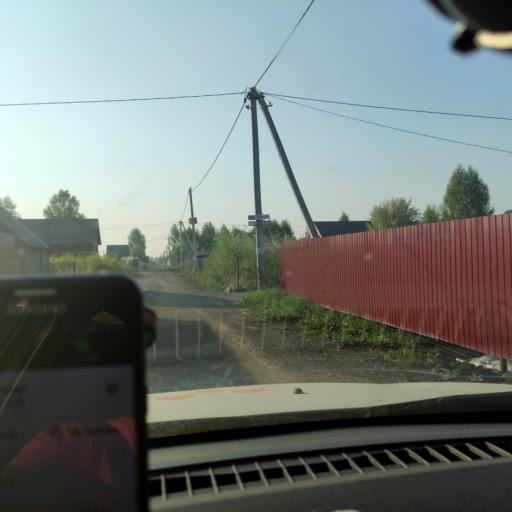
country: RU
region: Bashkortostan
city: Kabakovo
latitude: 54.7238
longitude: 56.2207
